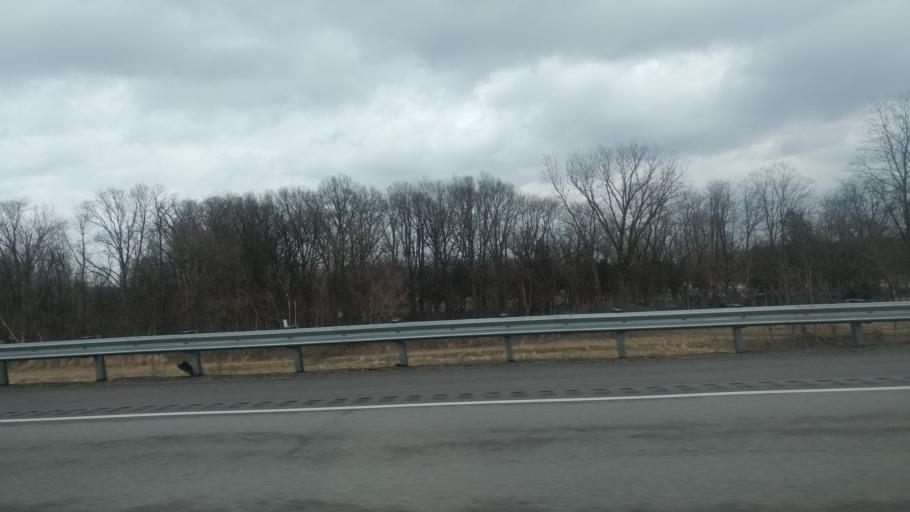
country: US
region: Ohio
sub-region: Lucas County
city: Maumee
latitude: 41.5480
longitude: -83.6836
